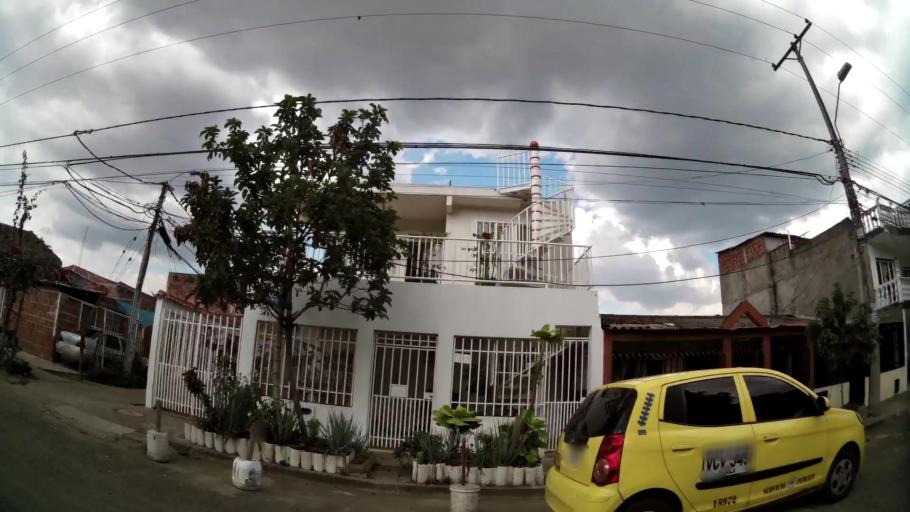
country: CO
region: Valle del Cauca
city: Cali
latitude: 3.4013
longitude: -76.5013
